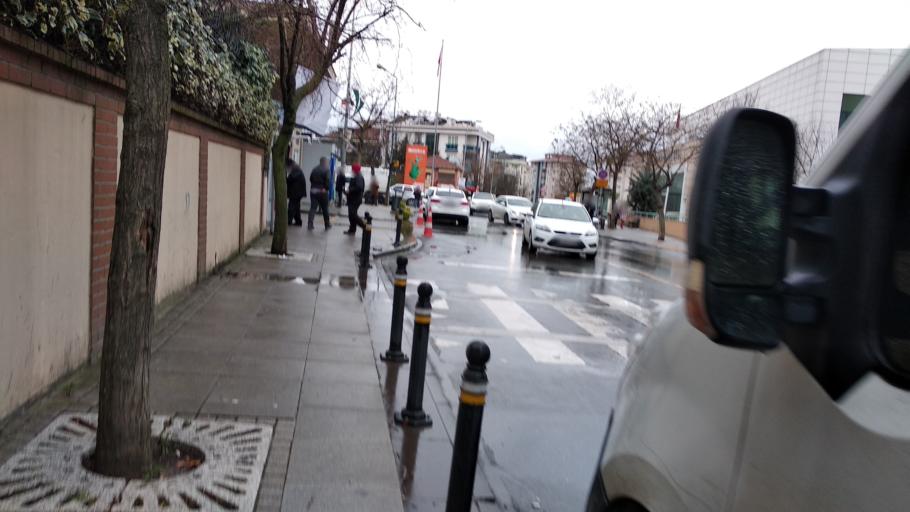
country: TR
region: Istanbul
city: Samandira
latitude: 41.0227
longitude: 29.1853
